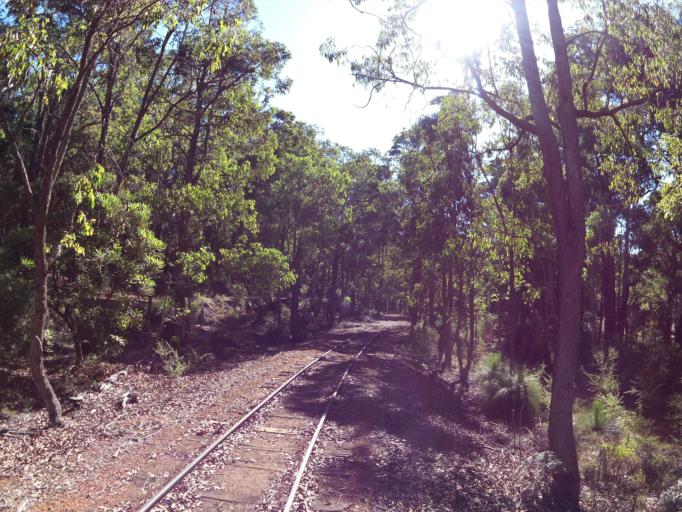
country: AU
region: Western Australia
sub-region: Waroona
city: Waroona
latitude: -32.7114
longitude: 116.0852
